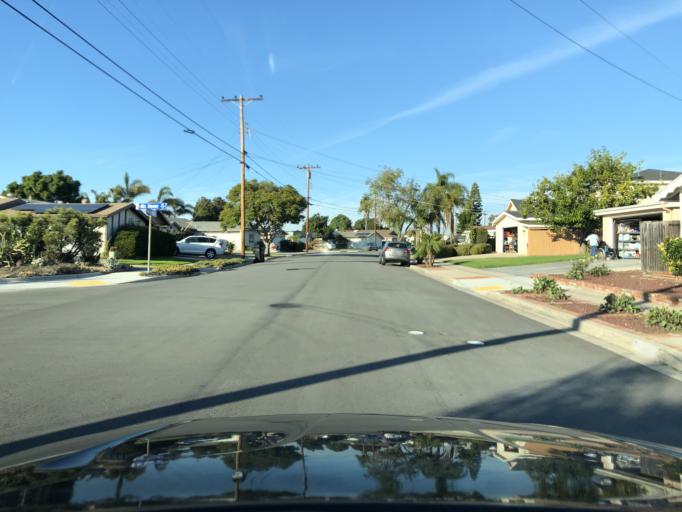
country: US
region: California
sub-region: San Diego County
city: La Jolla
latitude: 32.8204
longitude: -117.1957
